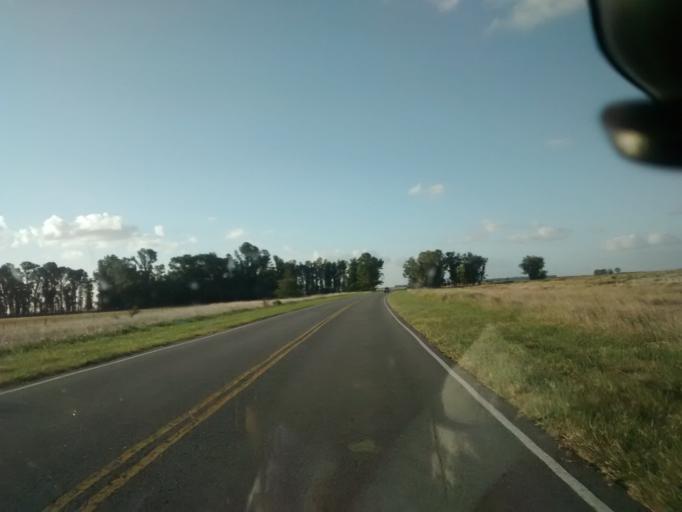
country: AR
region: Buenos Aires
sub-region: Partido de General Belgrano
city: General Belgrano
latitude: -36.1023
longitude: -58.6070
